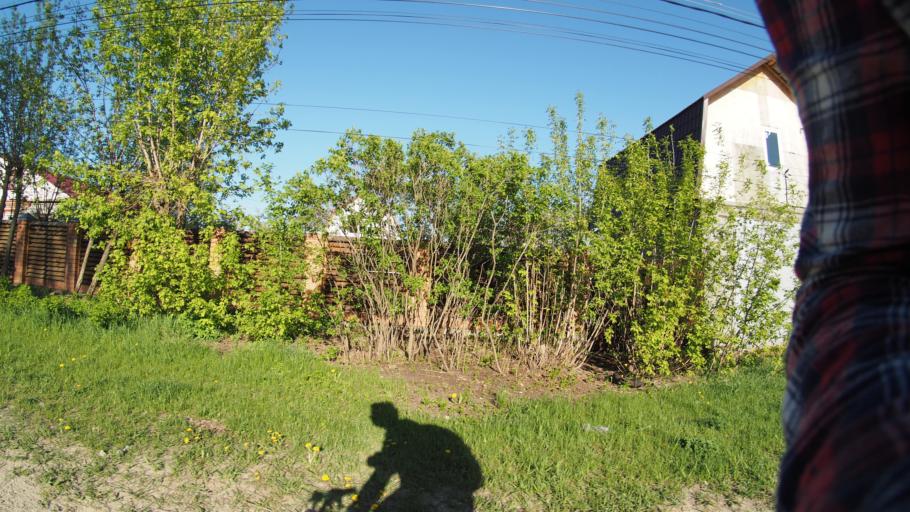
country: RU
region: Moskovskaya
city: Ramenskoye
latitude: 55.5490
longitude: 38.1963
